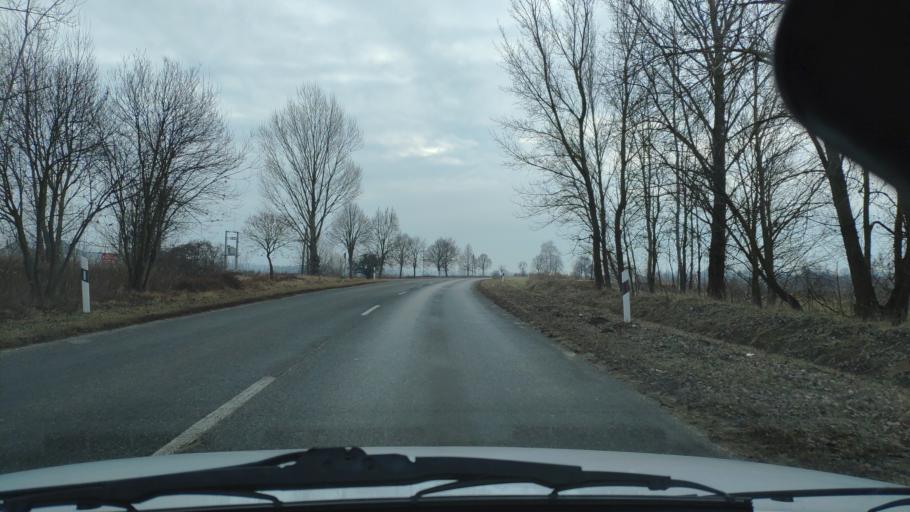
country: HU
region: Zala
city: Nagykanizsa
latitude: 46.5125
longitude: 16.9828
